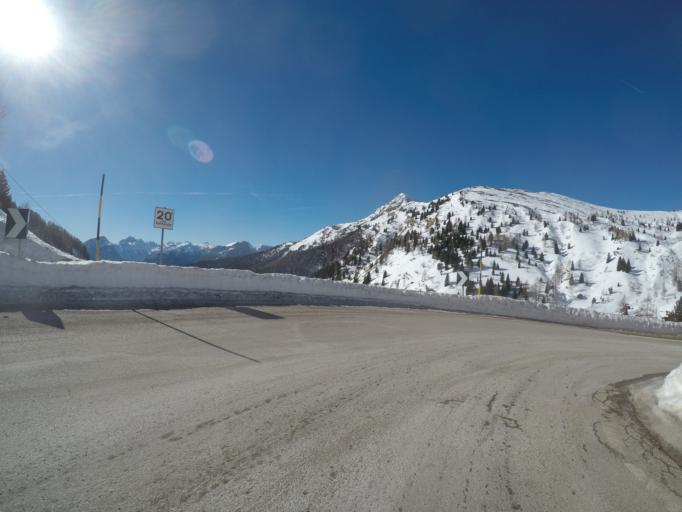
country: IT
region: Veneto
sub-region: Provincia di Belluno
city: Selva di Cadore
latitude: 46.4843
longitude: 12.0364
